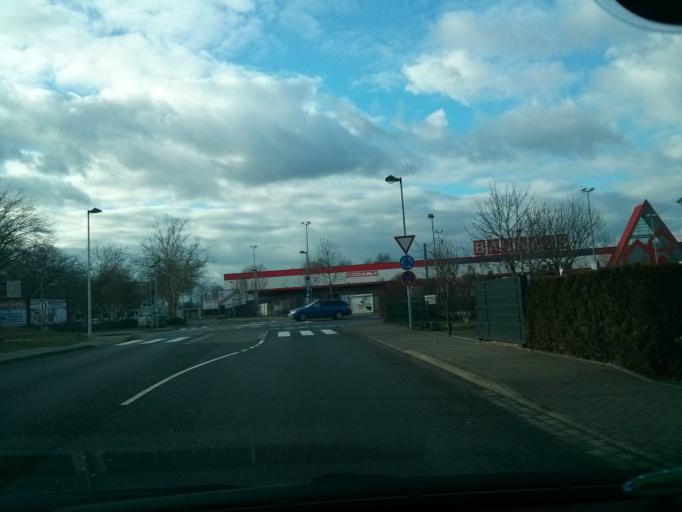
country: DE
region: North Rhine-Westphalia
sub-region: Regierungsbezirk Koln
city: Hennef
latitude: 50.7787
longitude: 7.2716
